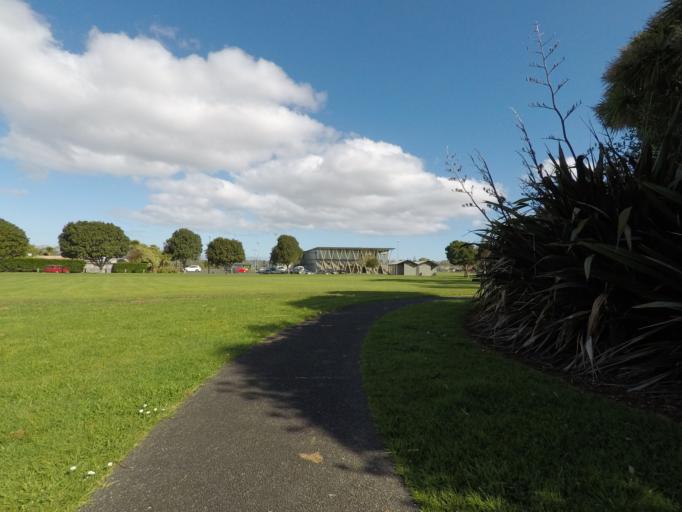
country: NZ
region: Auckland
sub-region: Auckland
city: Rosebank
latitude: -36.8585
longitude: 174.6046
